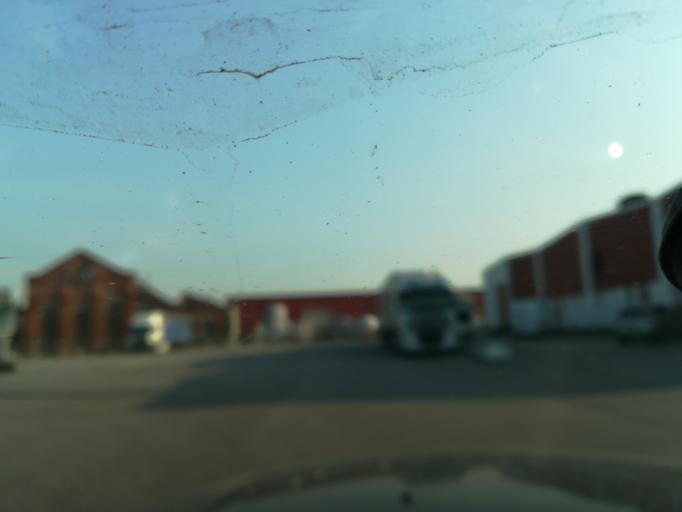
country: SE
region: Skane
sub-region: Ystads Kommun
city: Ystad
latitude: 55.4257
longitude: 13.8348
